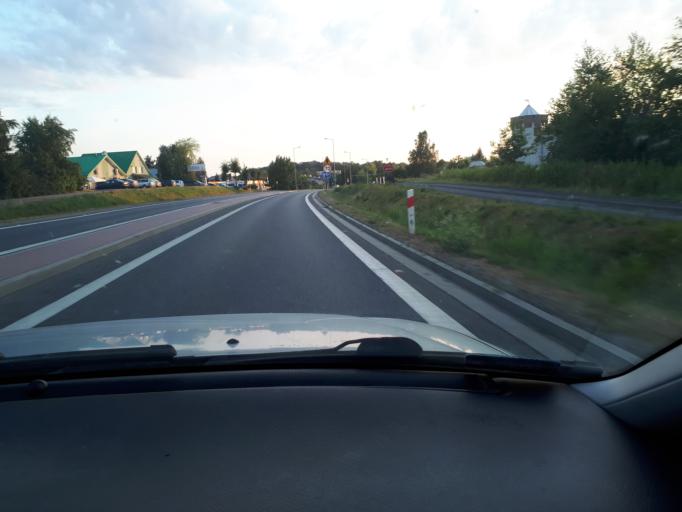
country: PL
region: Subcarpathian Voivodeship
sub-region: Powiat debicki
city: Debica
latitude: 50.0346
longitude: 21.4086
